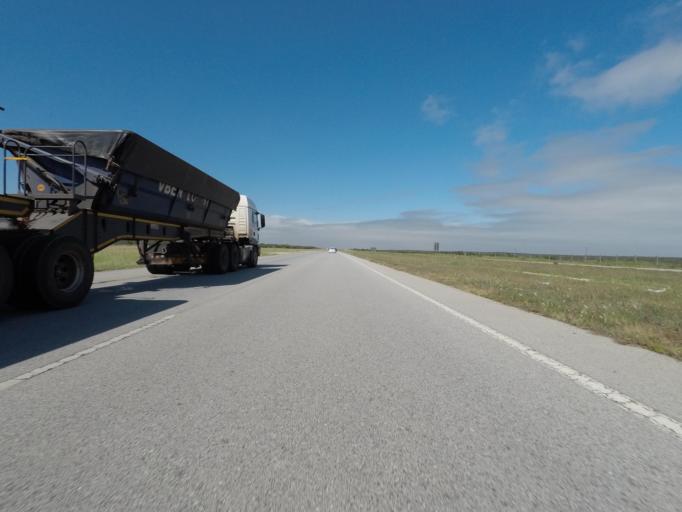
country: ZA
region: Eastern Cape
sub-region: Nelson Mandela Bay Metropolitan Municipality
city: Port Elizabeth
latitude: -33.7569
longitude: 25.6993
